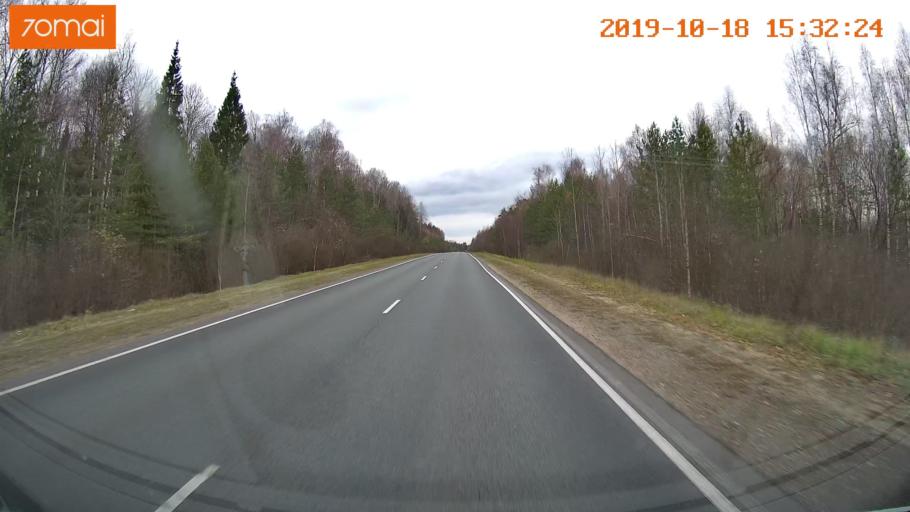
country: RU
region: Vladimir
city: Anopino
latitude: 55.8258
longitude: 40.6536
